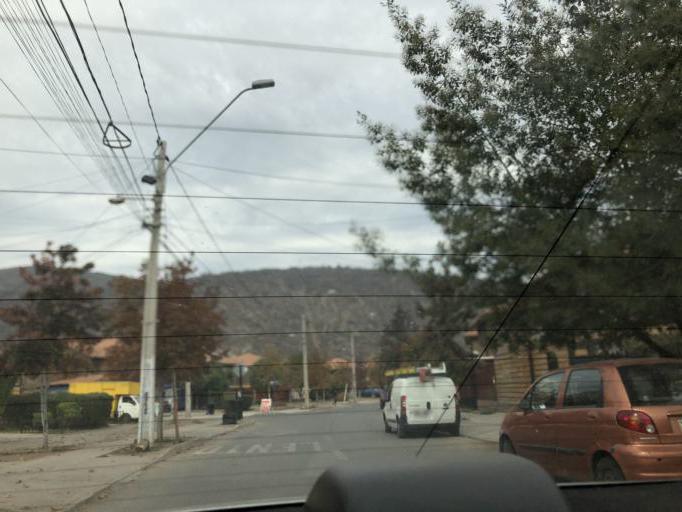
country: CL
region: Santiago Metropolitan
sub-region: Provincia de Cordillera
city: Puente Alto
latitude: -33.6128
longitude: -70.5237
